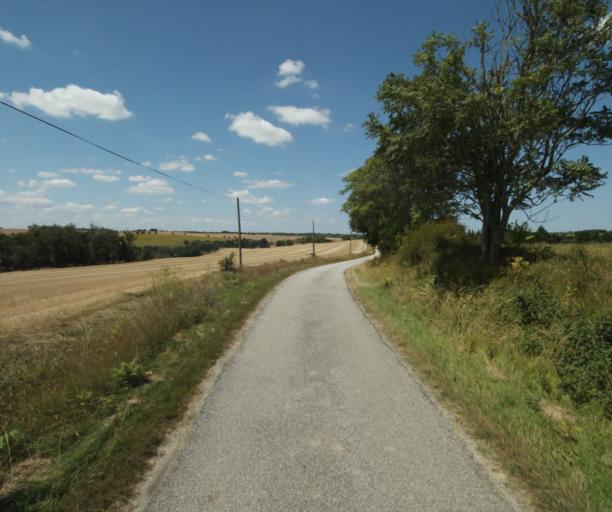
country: FR
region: Midi-Pyrenees
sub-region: Departement de la Haute-Garonne
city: Auriac-sur-Vendinelle
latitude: 43.5045
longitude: 1.8418
